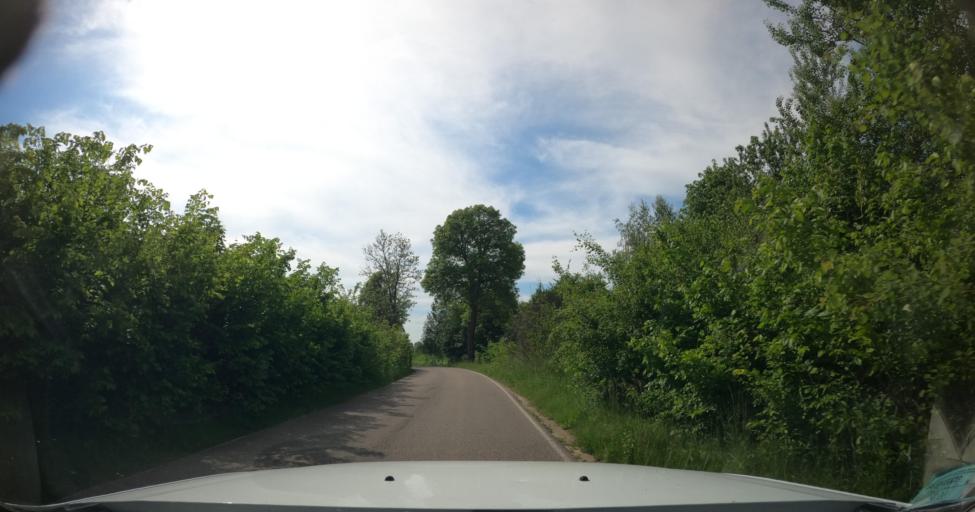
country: PL
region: Warmian-Masurian Voivodeship
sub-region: Powiat ostrodzki
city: Milakowo
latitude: 54.0094
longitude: 20.1325
